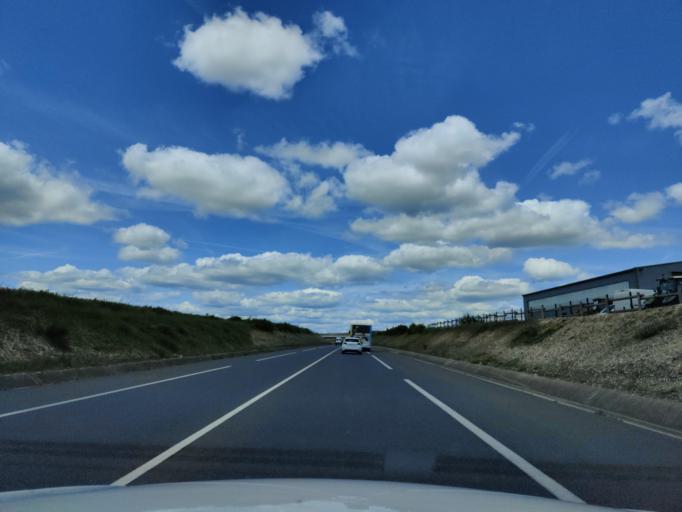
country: FR
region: Centre
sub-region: Departement du Cher
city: Fussy
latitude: 47.1118
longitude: 2.4466
